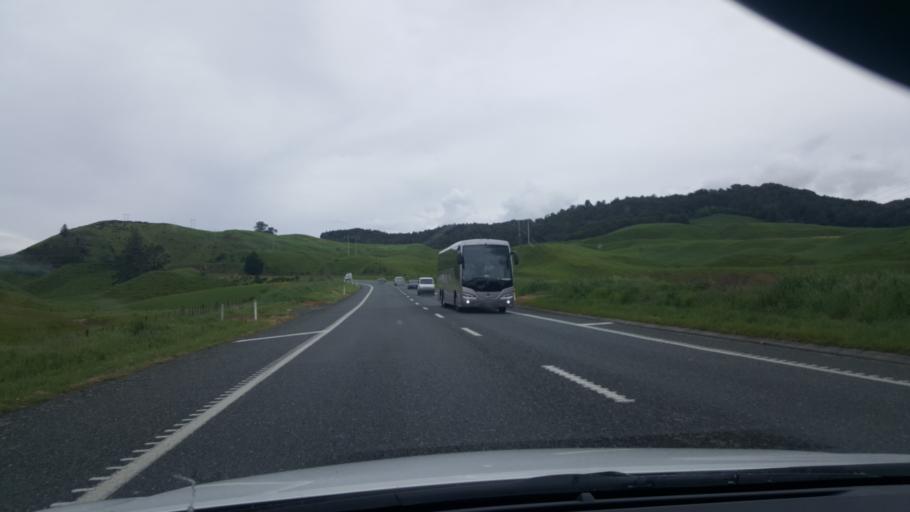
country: NZ
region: Bay of Plenty
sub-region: Rotorua District
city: Rotorua
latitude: -38.2599
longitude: 176.3200
